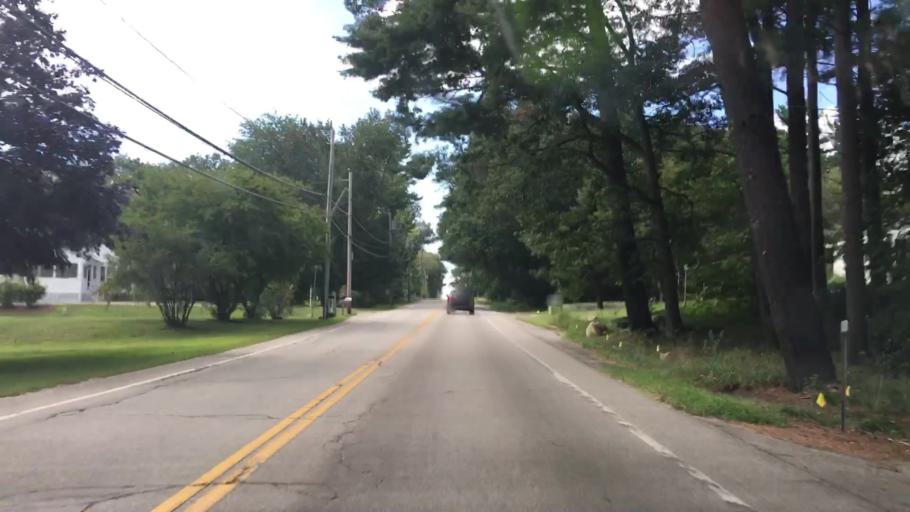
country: US
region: New Hampshire
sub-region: Strafford County
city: Somersworth
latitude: 43.2620
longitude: -70.8946
